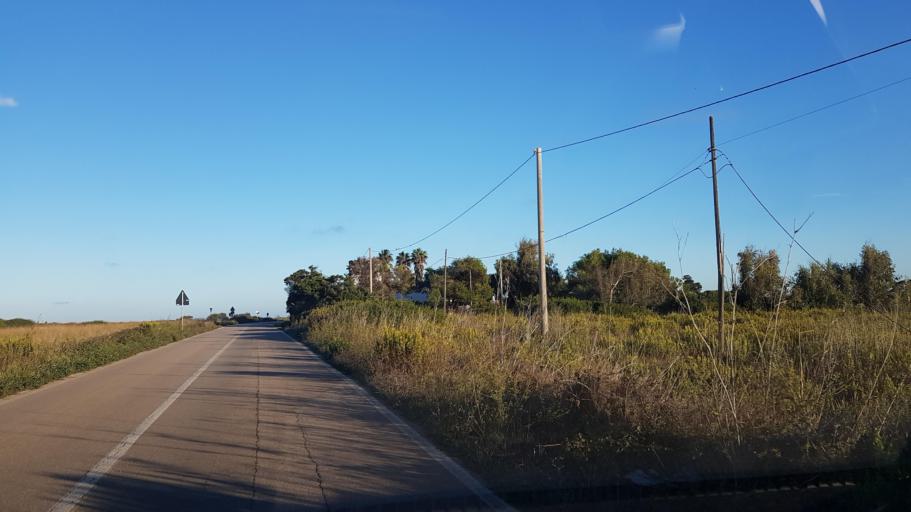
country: IT
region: Apulia
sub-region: Provincia di Lecce
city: Giorgilorio
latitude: 40.4494
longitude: 18.2253
